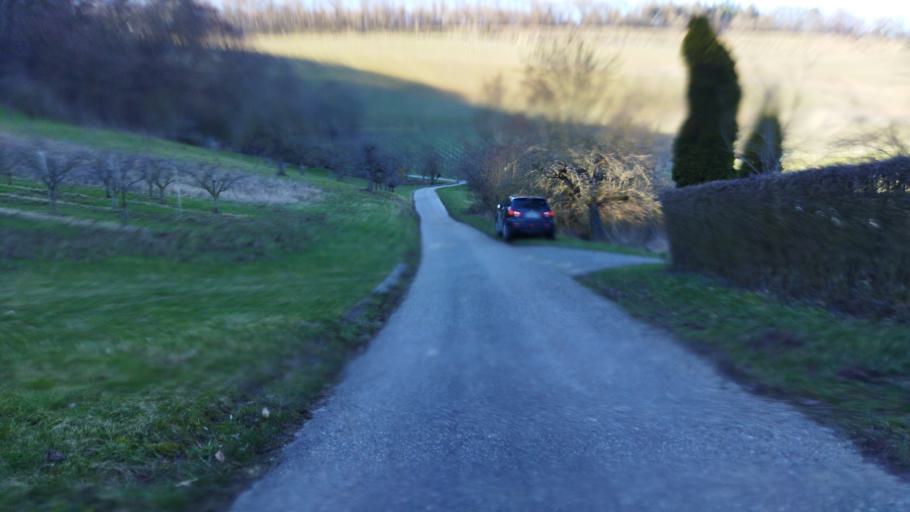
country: DE
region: Baden-Wuerttemberg
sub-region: Regierungsbezirk Stuttgart
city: Erlenbach
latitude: 49.1733
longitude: 9.2855
